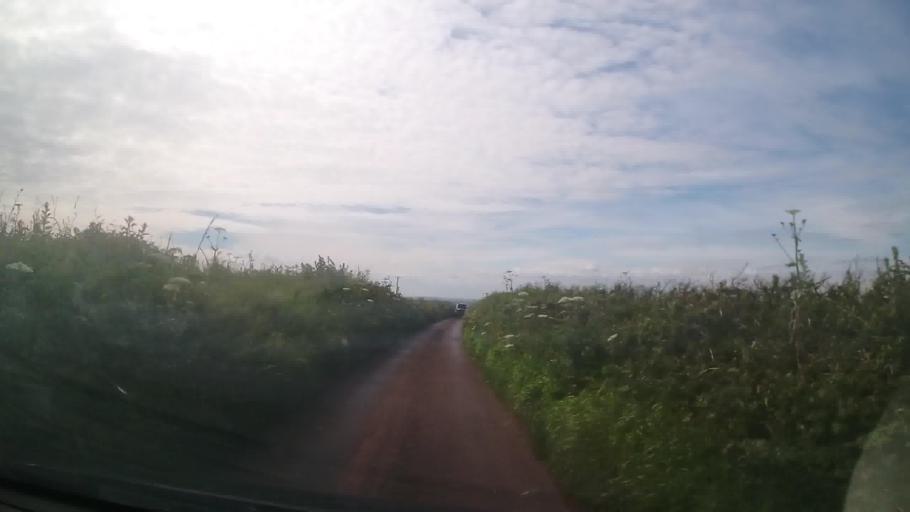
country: GB
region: England
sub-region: Devon
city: Salcombe
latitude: 50.2297
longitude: -3.6665
